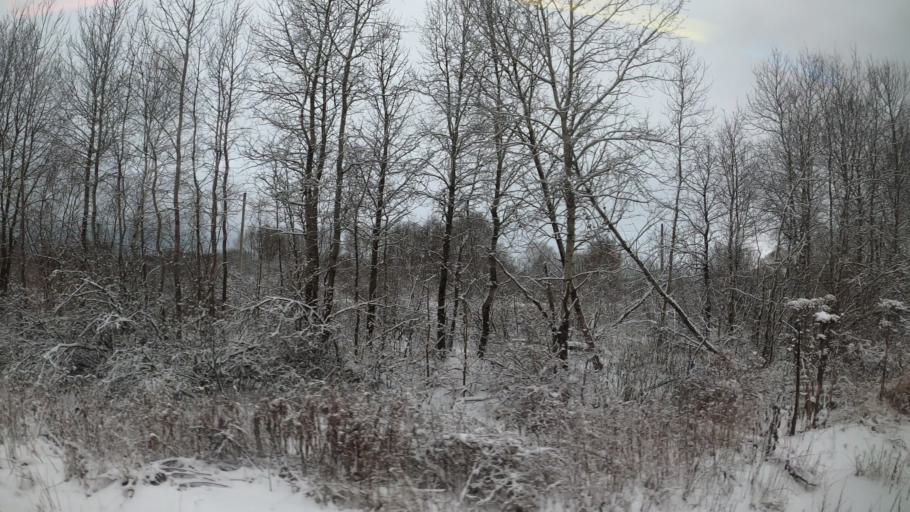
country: RU
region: Jaroslavl
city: Pereslavl'-Zalesskiy
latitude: 56.7319
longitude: 38.8999
